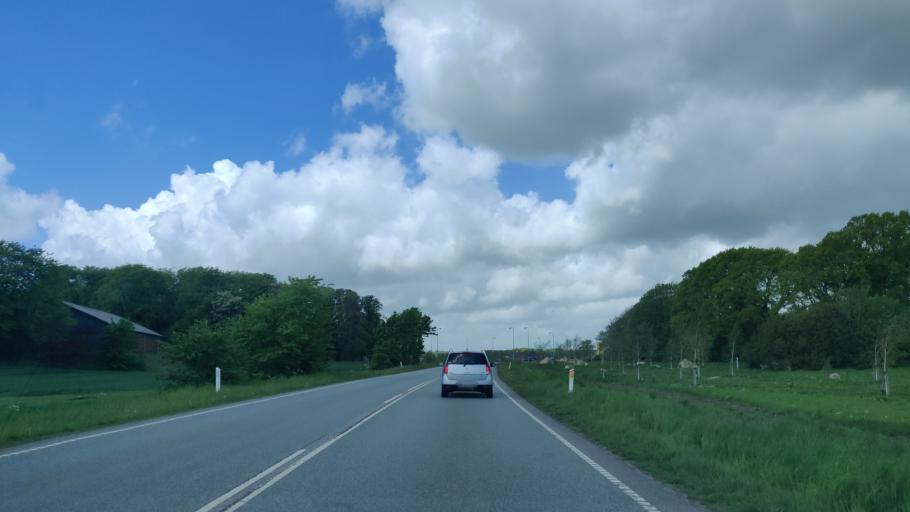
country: DK
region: Central Jutland
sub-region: Hedensted Kommune
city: Torring
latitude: 55.8471
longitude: 9.4787
